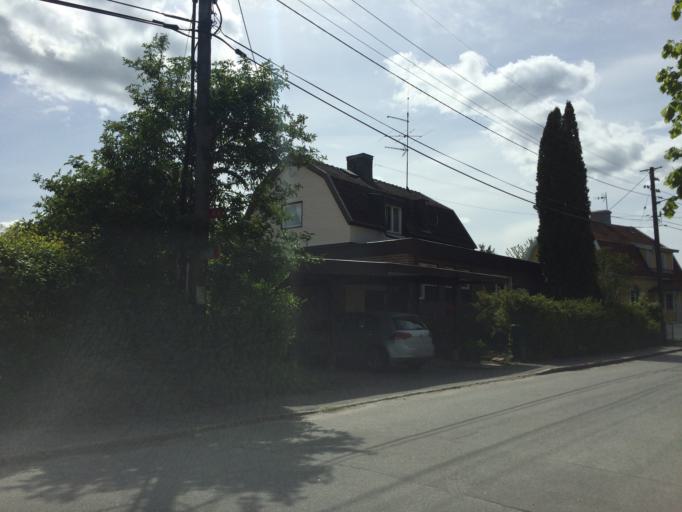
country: SE
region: Stockholm
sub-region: Huddinge Kommun
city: Huddinge
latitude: 59.2755
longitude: 18.0025
